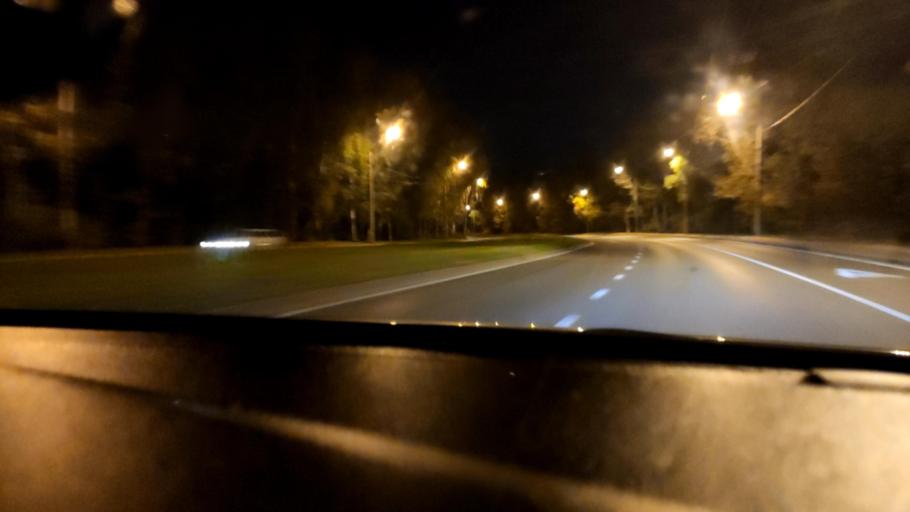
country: RU
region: Tatarstan
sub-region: Gorod Kazan'
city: Kazan
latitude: 55.7569
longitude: 49.1754
